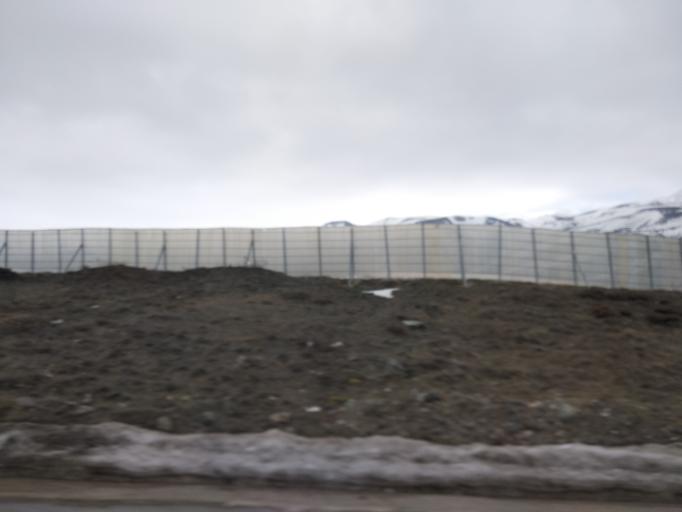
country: TR
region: Erzincan
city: Catalarmut
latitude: 39.8256
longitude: 39.3939
